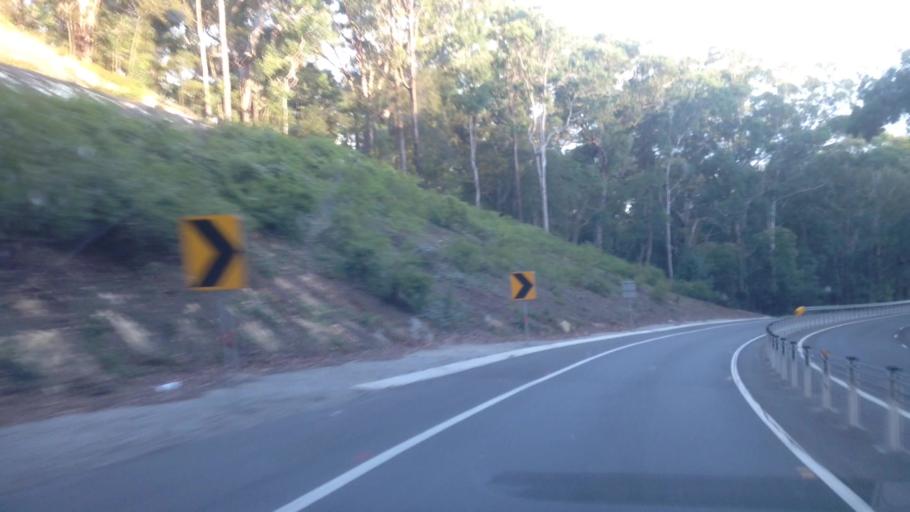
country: AU
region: New South Wales
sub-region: Lake Macquarie Shire
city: Cooranbong
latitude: -32.9706
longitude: 151.4823
